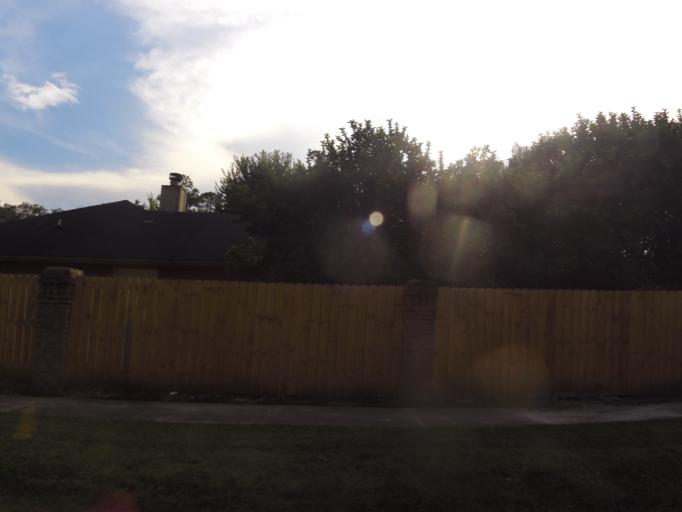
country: US
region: Florida
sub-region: Saint Johns County
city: Fruit Cove
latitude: 30.1520
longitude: -81.5974
